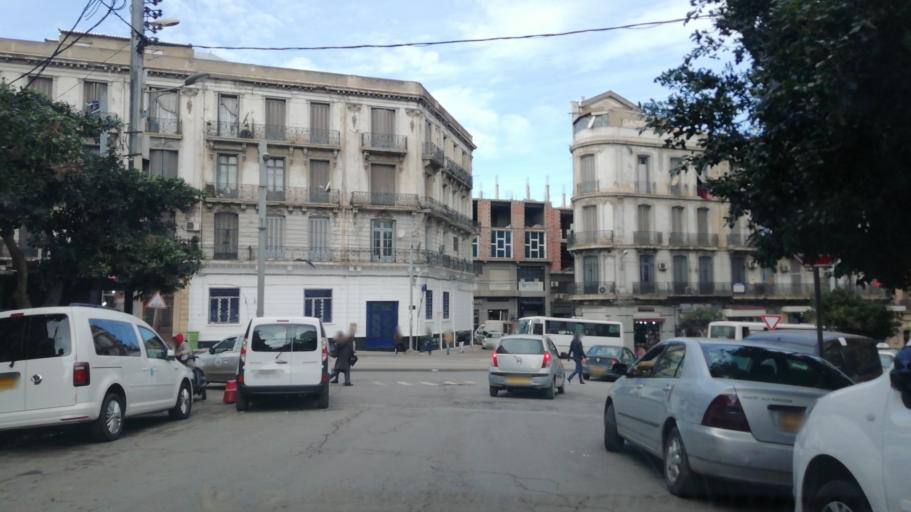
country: DZ
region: Oran
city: Oran
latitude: 35.6978
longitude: -0.6507
